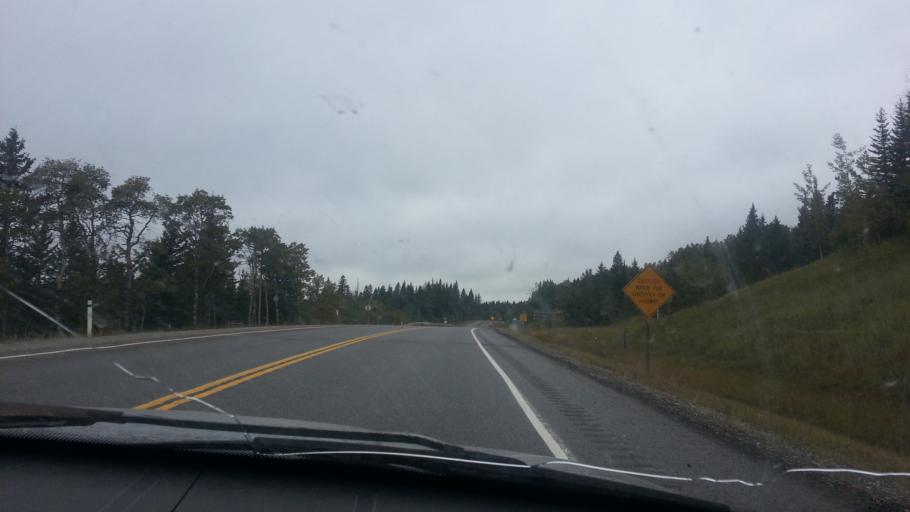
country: CA
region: Alberta
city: Cochrane
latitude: 51.0368
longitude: -114.7219
